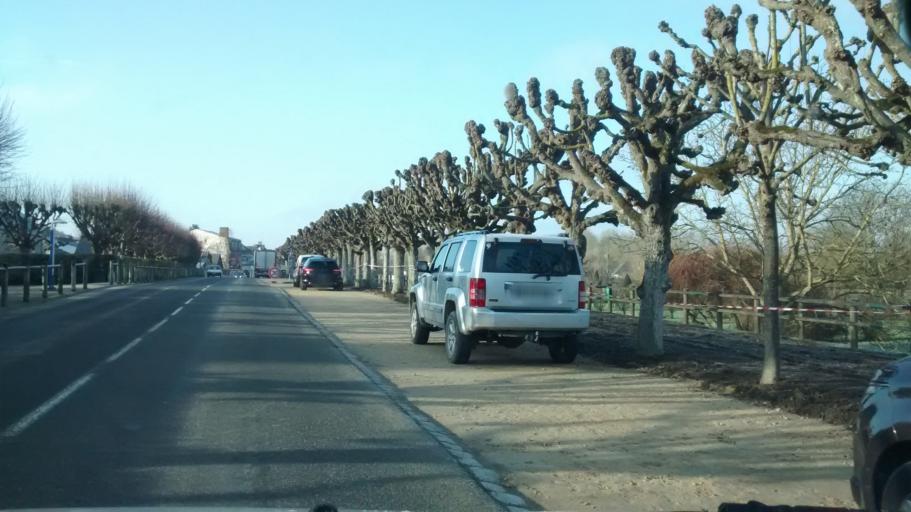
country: FR
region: Centre
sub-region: Departement d'Indre-et-Loire
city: Villandry
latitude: 47.3415
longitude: 0.5141
